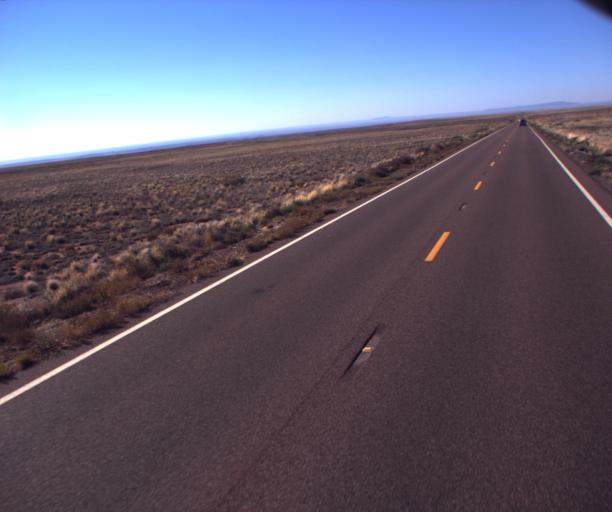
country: US
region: Arizona
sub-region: Navajo County
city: Joseph City
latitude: 35.1398
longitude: -110.4849
